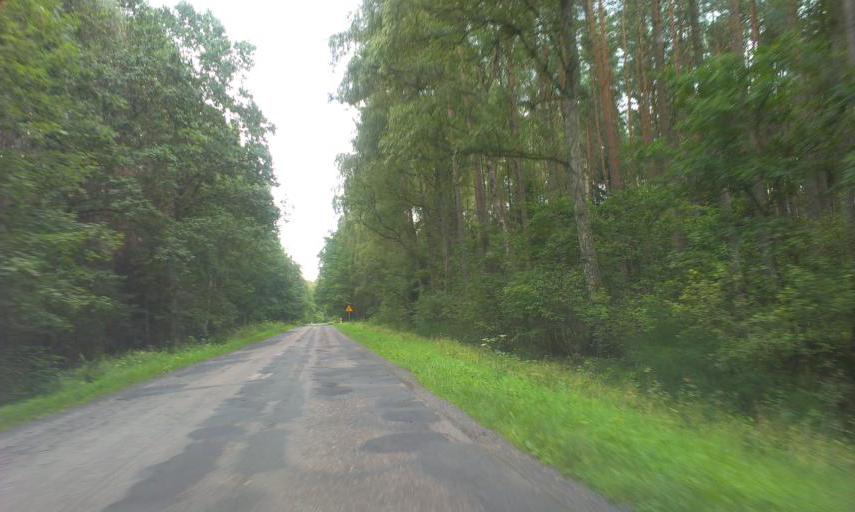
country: PL
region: West Pomeranian Voivodeship
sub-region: Powiat bialogardzki
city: Tychowo
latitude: 53.9915
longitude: 16.1822
